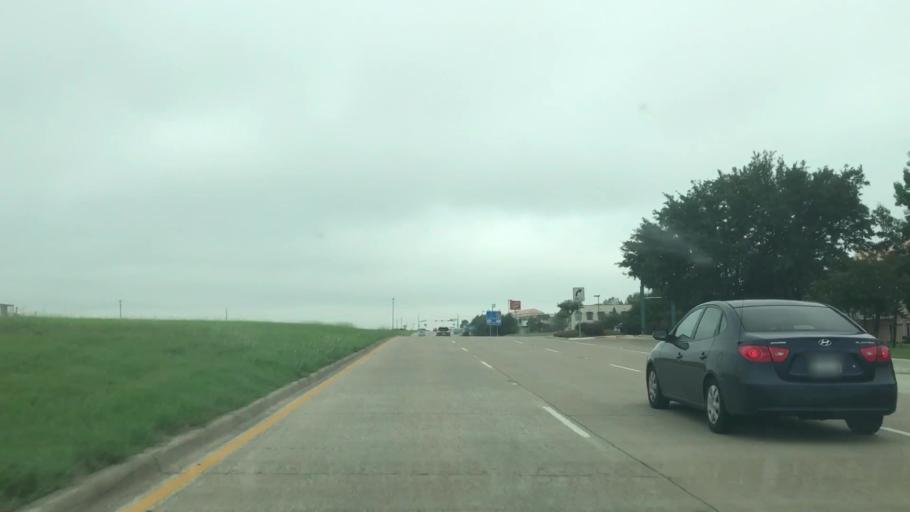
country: US
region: Texas
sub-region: Dallas County
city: Farmers Branch
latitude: 32.9151
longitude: -96.9537
